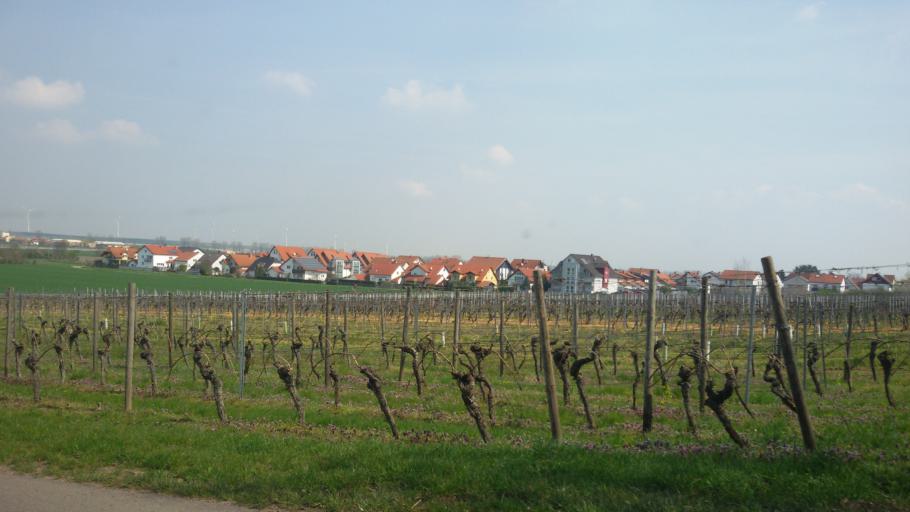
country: DE
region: Rheinland-Pfalz
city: Gerolsheim
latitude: 49.5453
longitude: 8.2535
